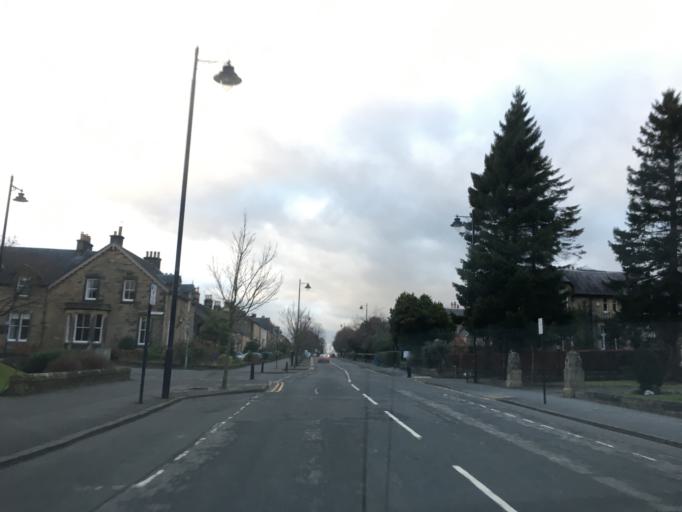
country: GB
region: Scotland
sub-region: Stirling
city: Stirling
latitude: 56.1180
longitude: -3.9426
